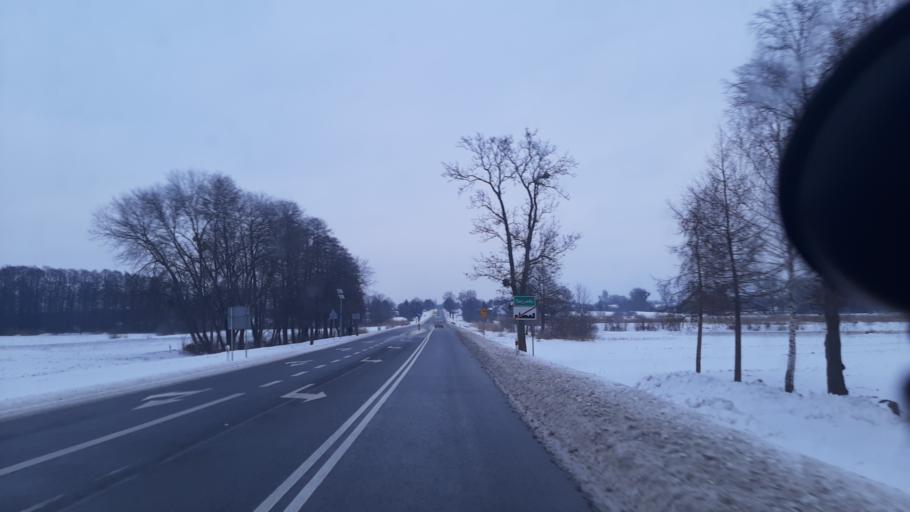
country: PL
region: Lublin Voivodeship
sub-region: Powiat lubelski
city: Garbow
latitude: 51.3621
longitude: 22.3054
